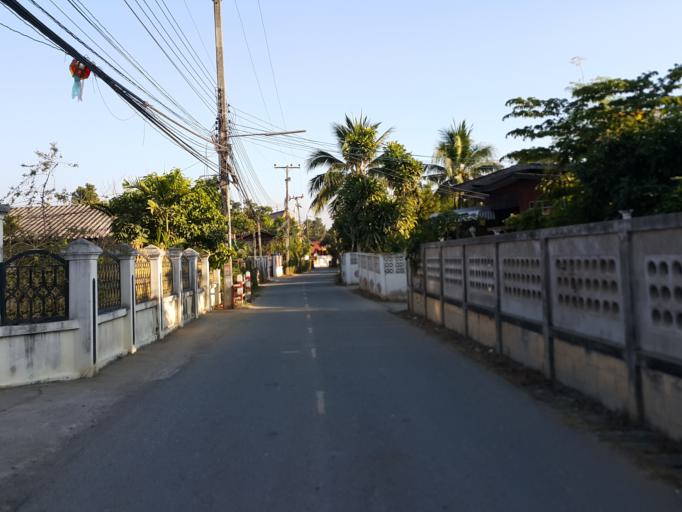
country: TH
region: Chiang Mai
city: San Kamphaeng
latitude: 18.7912
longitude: 99.1081
